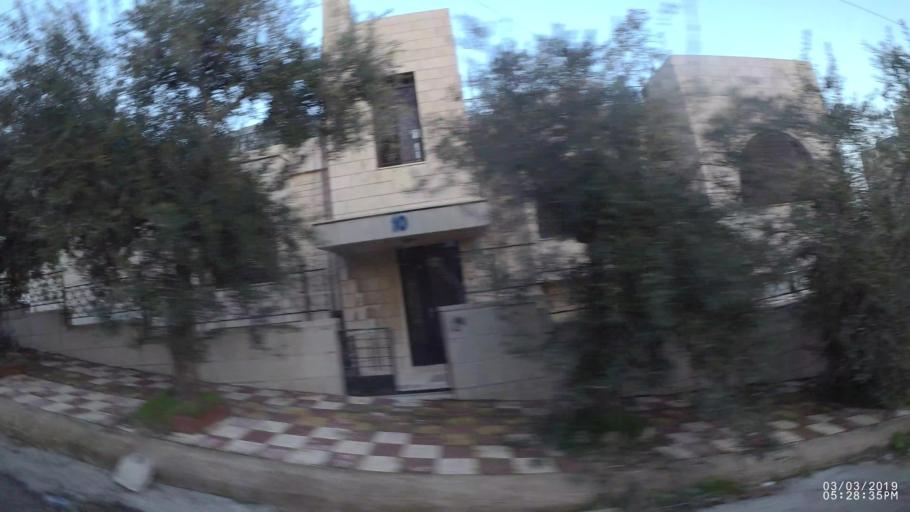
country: JO
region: Amman
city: Al Jubayhah
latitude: 31.9894
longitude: 35.8843
